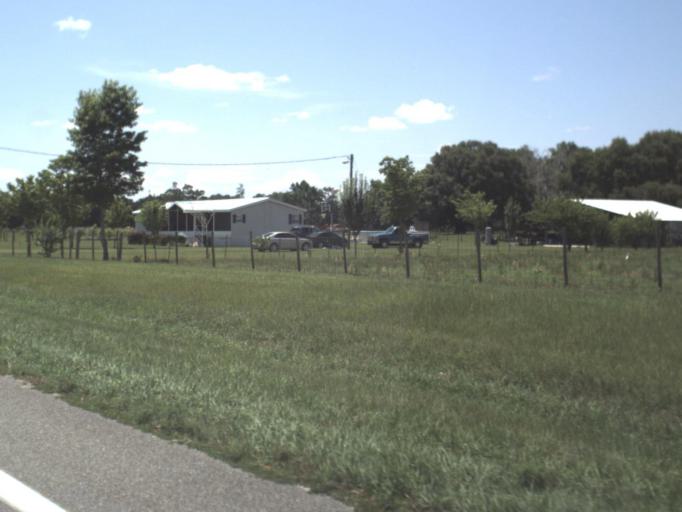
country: US
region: Florida
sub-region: Lafayette County
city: Mayo
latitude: 30.0533
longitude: -83.1080
